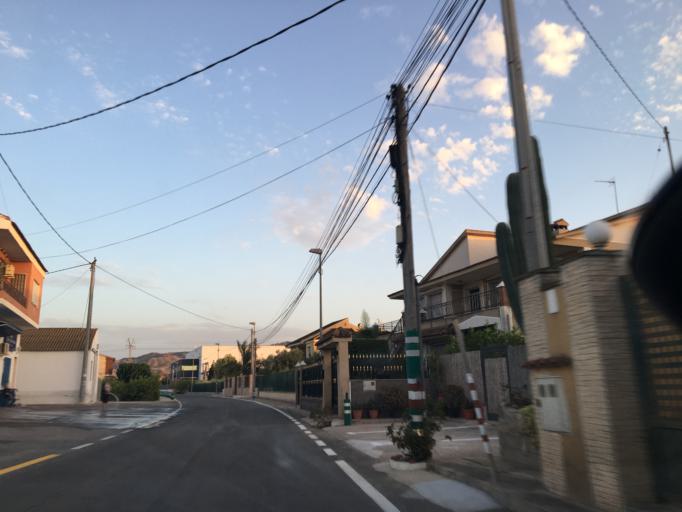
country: ES
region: Murcia
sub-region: Murcia
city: Santomera
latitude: 38.0214
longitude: -1.0537
